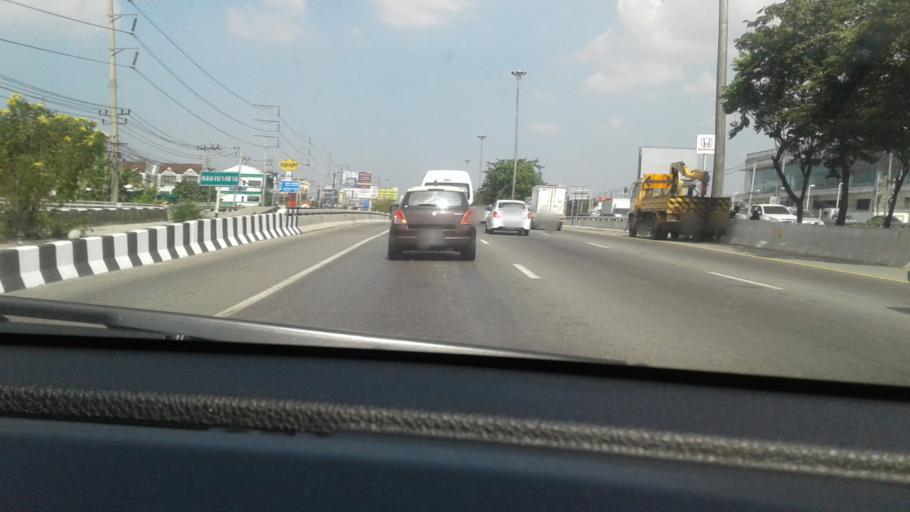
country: TH
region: Bangkok
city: Taling Chan
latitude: 13.7934
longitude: 100.4100
